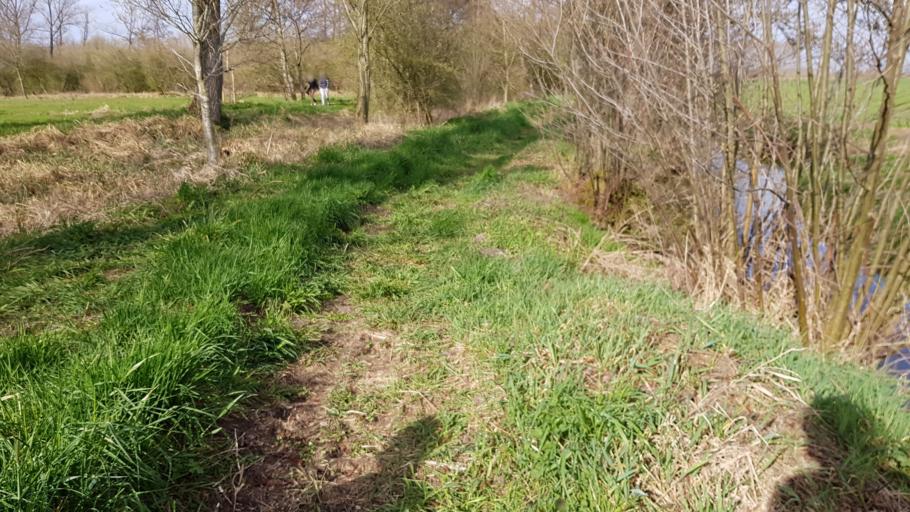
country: NL
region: Utrecht
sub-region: Gemeente Lopik
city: Lopik
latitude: 51.9543
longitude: 5.0026
